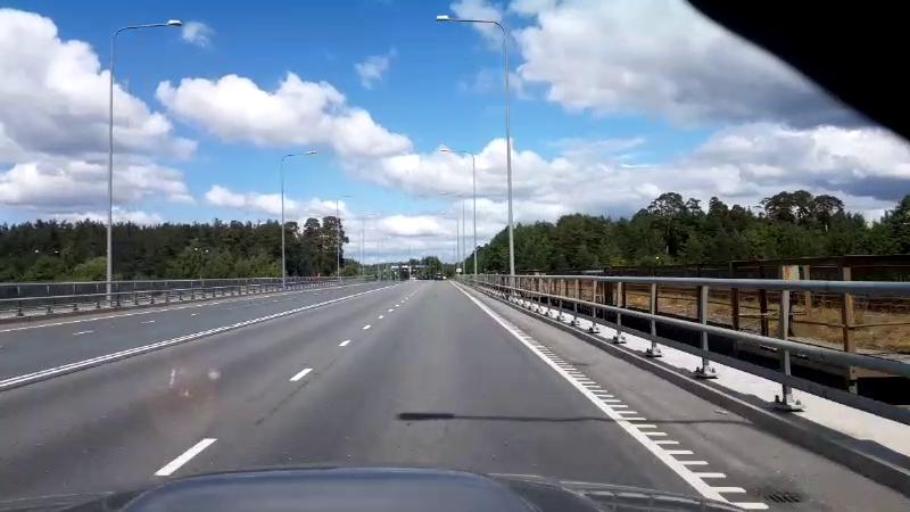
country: EE
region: Paernumaa
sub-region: Paernu linn
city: Parnu
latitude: 58.3795
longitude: 24.5561
